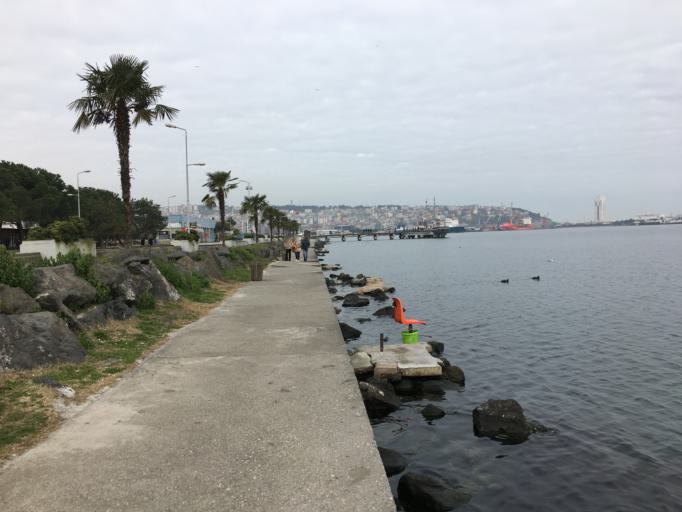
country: TR
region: Samsun
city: Samsun
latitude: 41.2912
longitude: 36.3415
